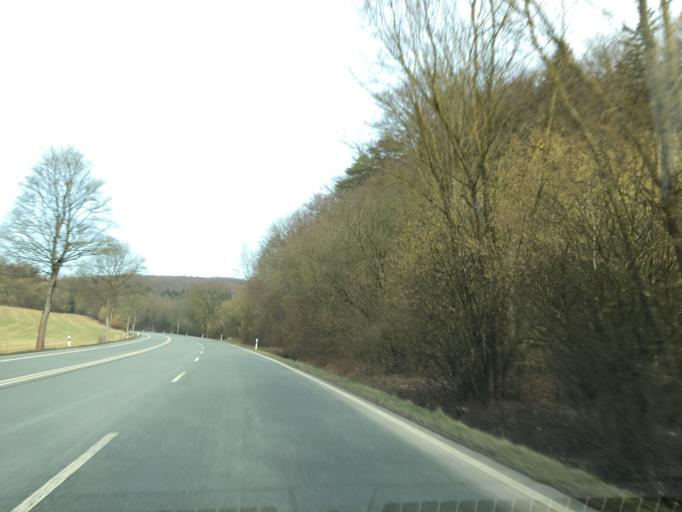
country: DE
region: North Rhine-Westphalia
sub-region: Regierungsbezirk Detmold
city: Willebadessen
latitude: 51.5495
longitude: 9.0139
